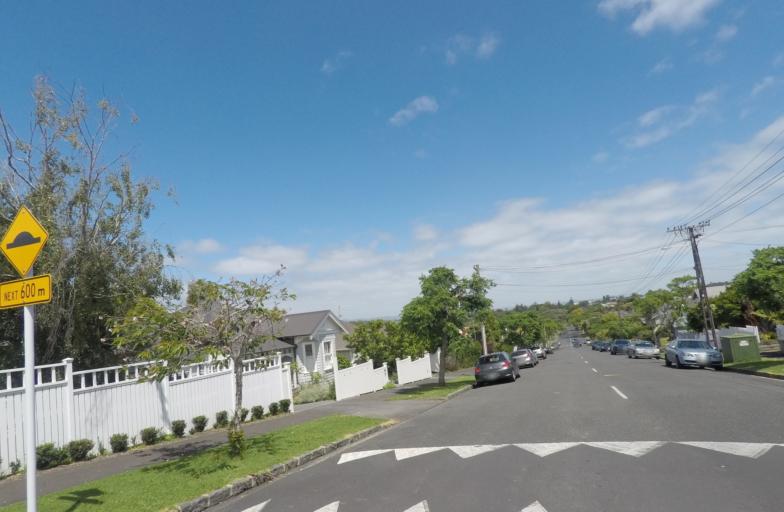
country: NZ
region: Auckland
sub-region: Auckland
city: Auckland
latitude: -36.8817
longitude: 174.7477
